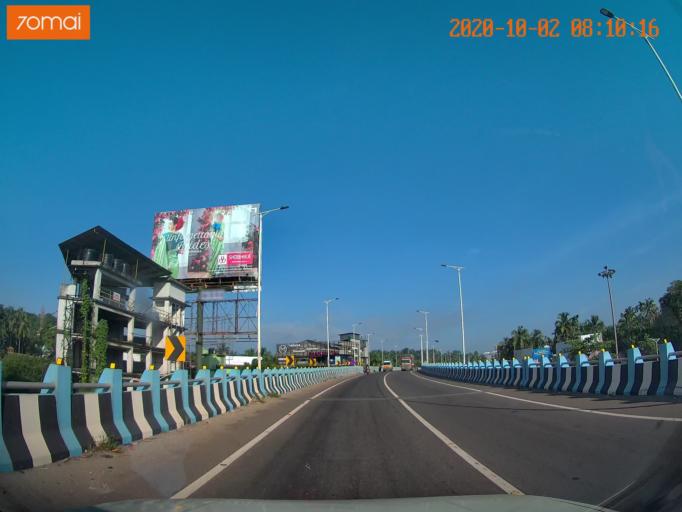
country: IN
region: Kerala
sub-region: Kozhikode
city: Kozhikode
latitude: 11.2644
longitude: 75.8120
